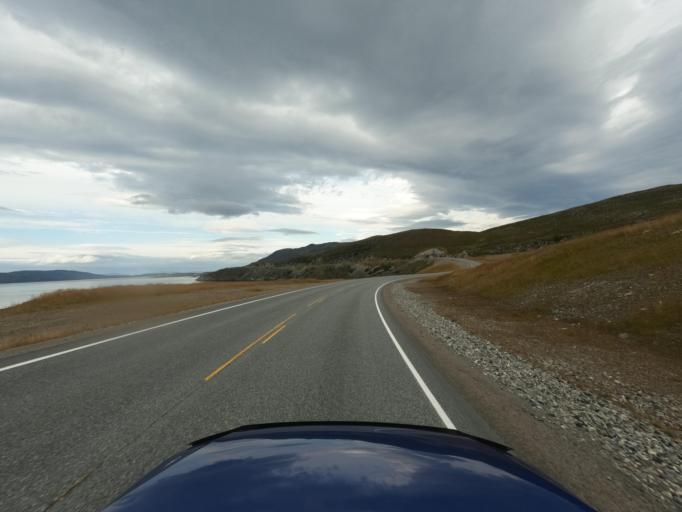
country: NO
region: Finnmark Fylke
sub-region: Hammerfest
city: Rypefjord
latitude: 70.5259
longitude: 23.7404
